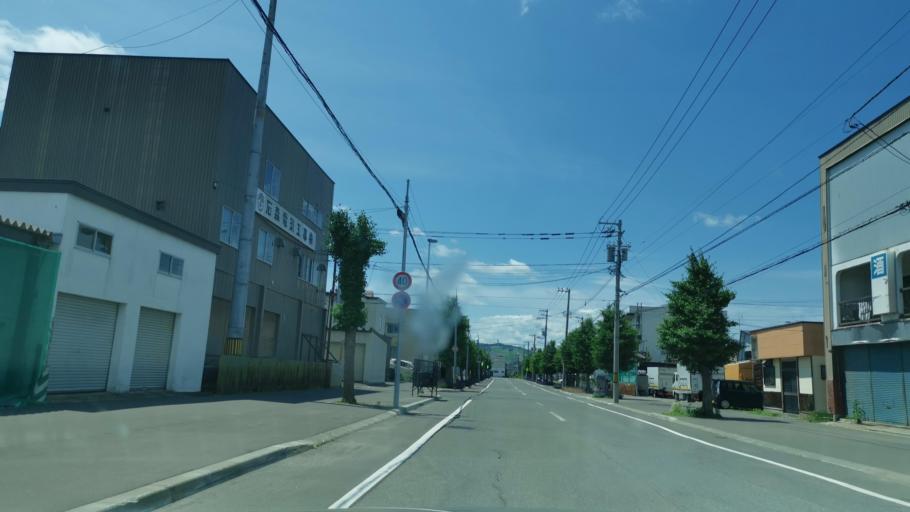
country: JP
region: Hokkaido
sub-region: Asahikawa-shi
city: Asahikawa
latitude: 43.7898
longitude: 142.3431
